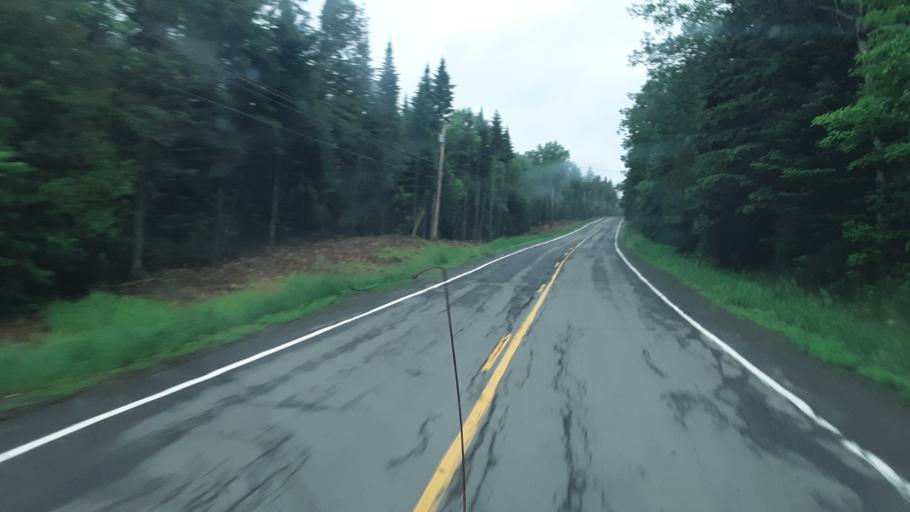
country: US
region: Maine
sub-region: Penobscot County
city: Patten
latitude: 46.1692
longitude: -68.3420
